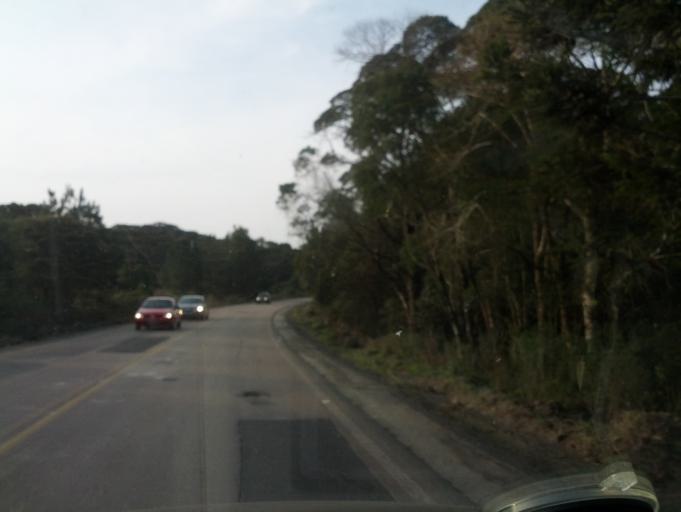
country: BR
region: Santa Catarina
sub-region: Otacilio Costa
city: Otacilio Costa
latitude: -27.3629
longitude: -50.1347
